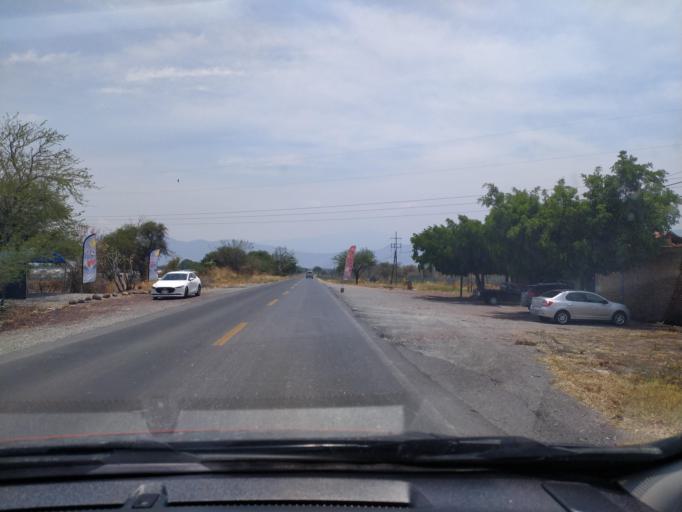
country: MX
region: Jalisco
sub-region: Zacoalco de Torres
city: Barranca de Otates (Barranca de Otatan)
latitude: 20.2794
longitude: -103.6239
